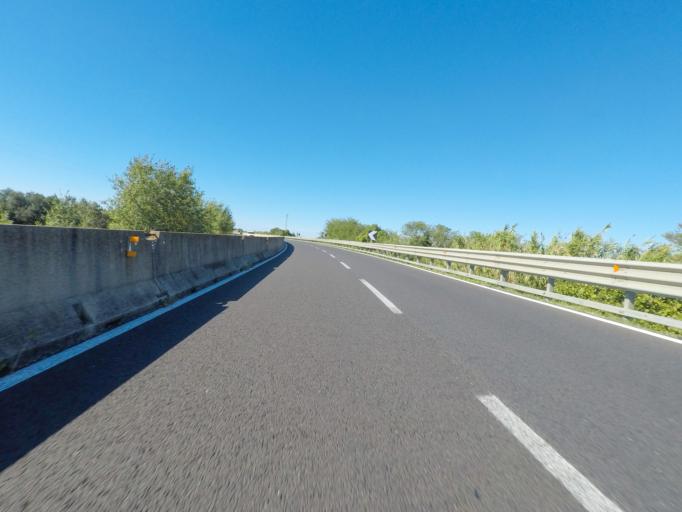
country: IT
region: Tuscany
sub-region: Provincia di Grosseto
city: Albinia
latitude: 42.4775
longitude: 11.2308
